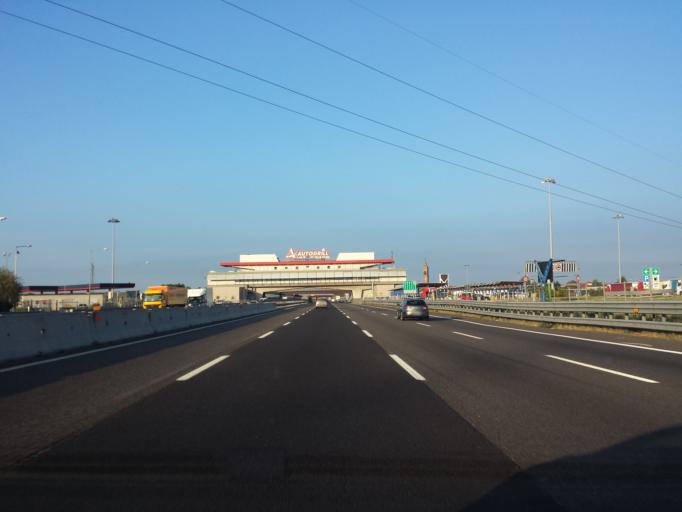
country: IT
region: Lombardy
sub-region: Provincia di Bergamo
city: Dalmine
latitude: 45.6335
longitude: 9.6014
